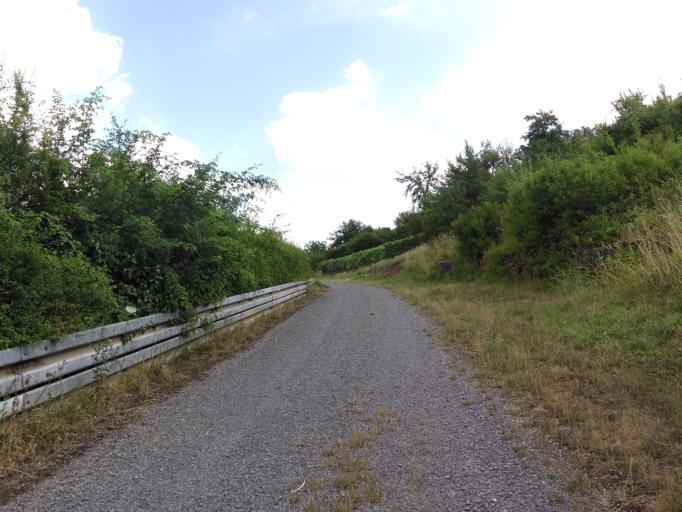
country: DE
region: Bavaria
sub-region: Regierungsbezirk Unterfranken
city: Randersacker
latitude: 49.7552
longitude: 9.9658
